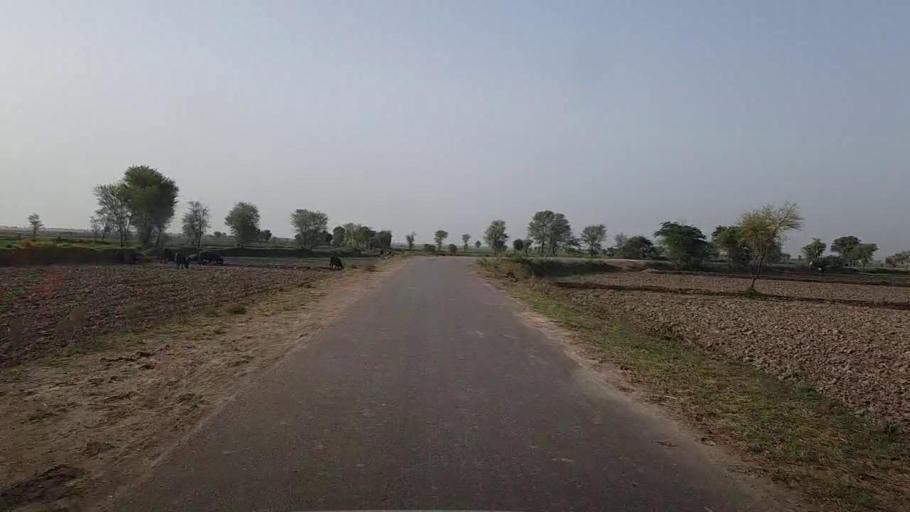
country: PK
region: Sindh
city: Khairpur Nathan Shah
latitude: 27.1043
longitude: 67.7940
